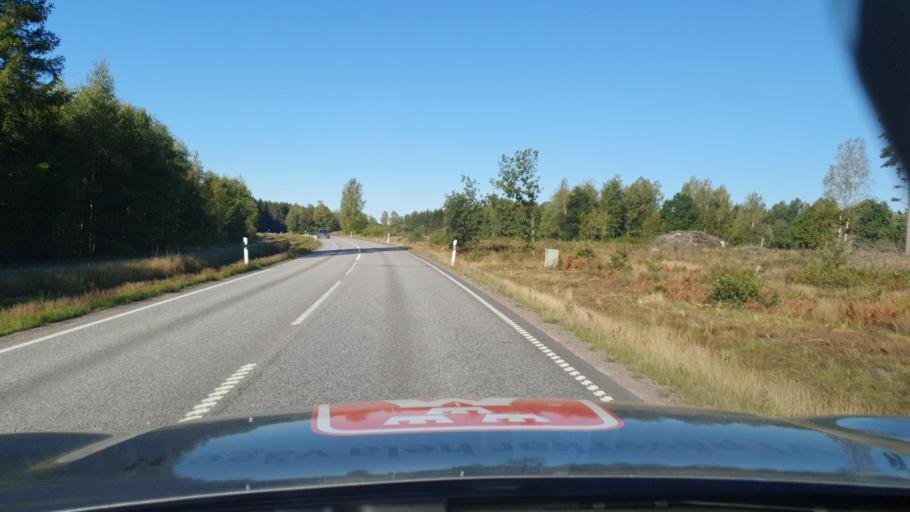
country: SE
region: OEstergoetland
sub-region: Finspangs Kommun
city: Finspang
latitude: 58.7271
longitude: 15.6231
